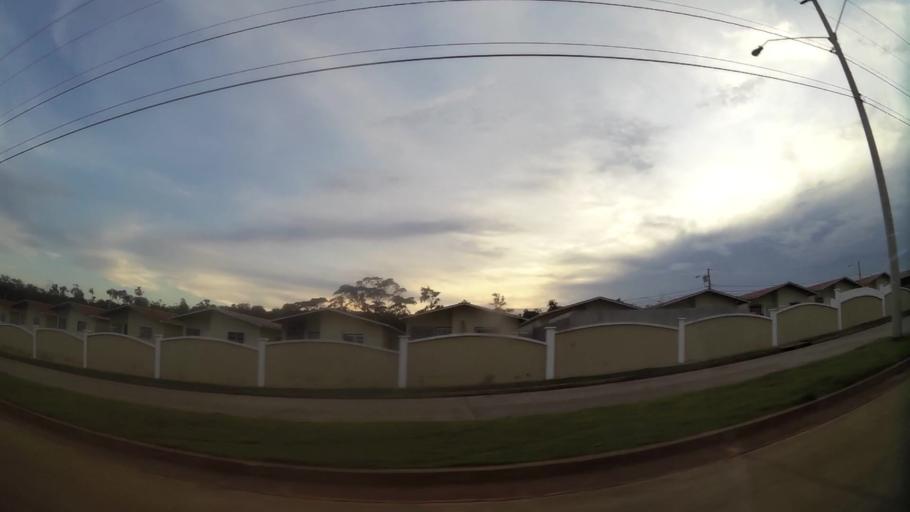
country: PA
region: Panama
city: La Mitra
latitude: 8.8590
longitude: -79.7627
